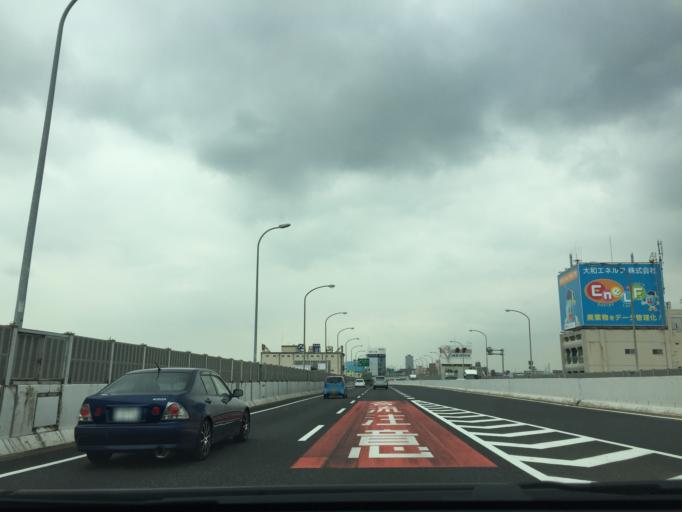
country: JP
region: Aichi
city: Nagoya-shi
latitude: 35.1012
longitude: 136.9255
